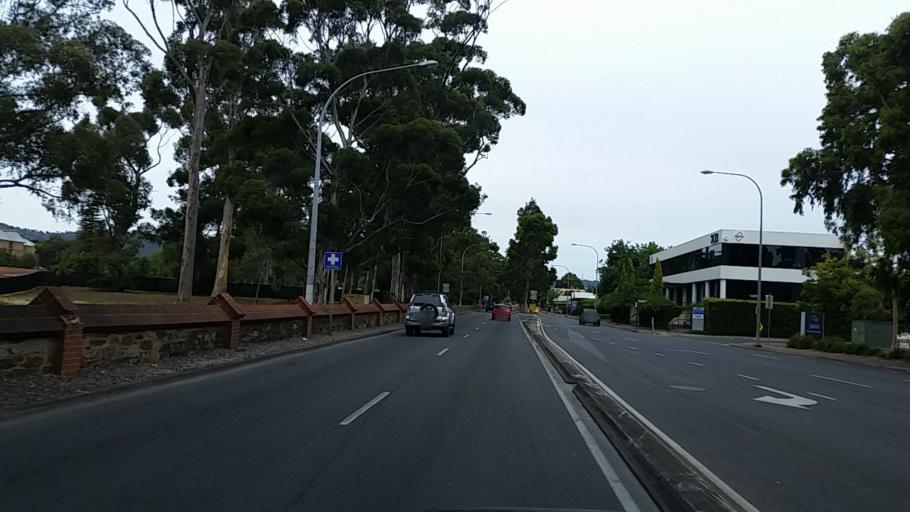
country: AU
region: South Australia
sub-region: Unley
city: Fullarton
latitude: -34.9405
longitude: 138.6246
